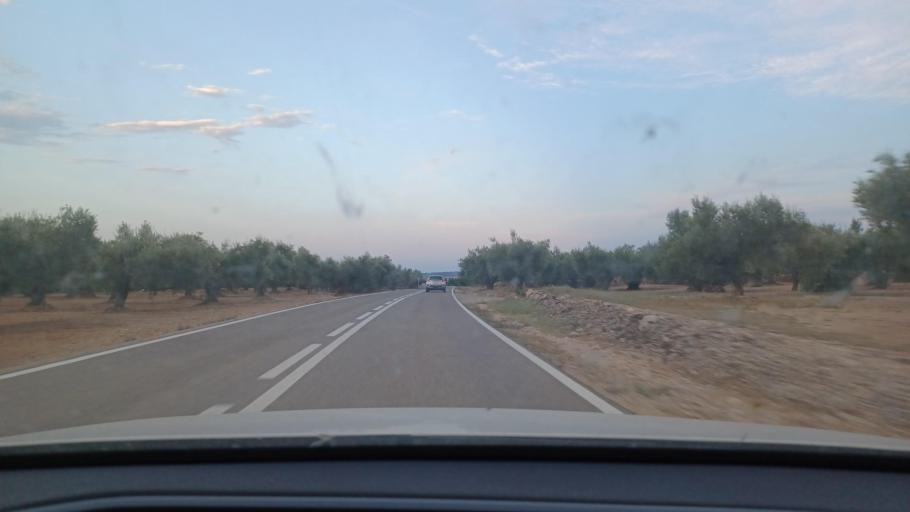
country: ES
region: Catalonia
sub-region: Provincia de Tarragona
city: Santa Barbara
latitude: 40.7198
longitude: 0.4616
